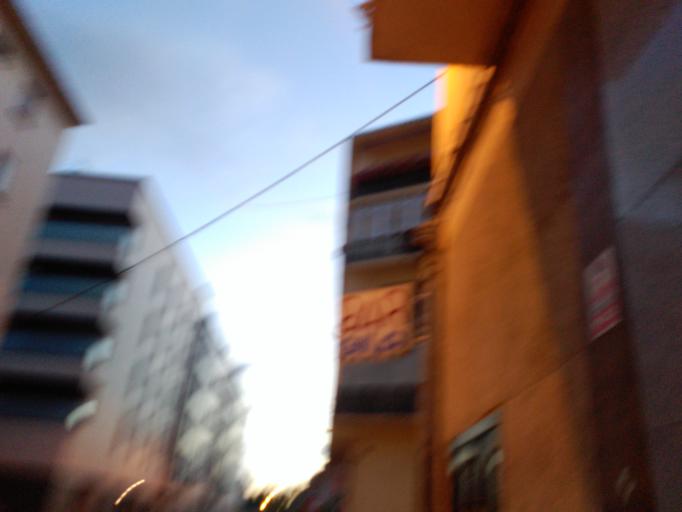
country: ES
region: Navarre
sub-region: Provincia de Navarra
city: Burlata
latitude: 42.8228
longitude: -1.6155
